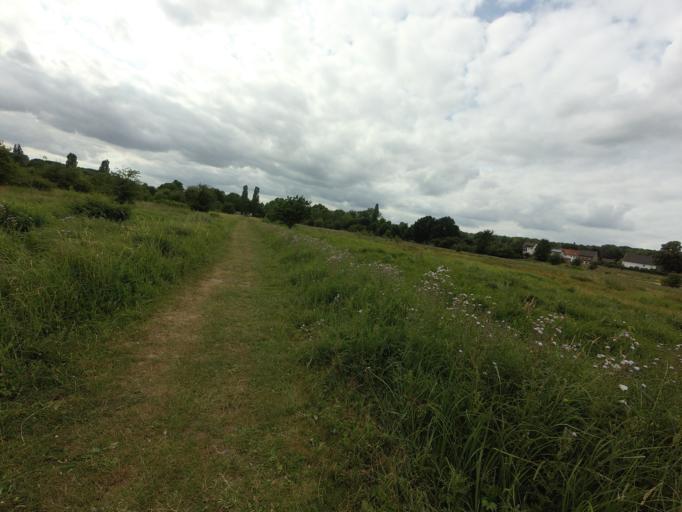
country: NL
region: Limburg
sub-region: Valkenburg aan de Geul
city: Houthem
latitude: 50.8694
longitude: 5.8041
